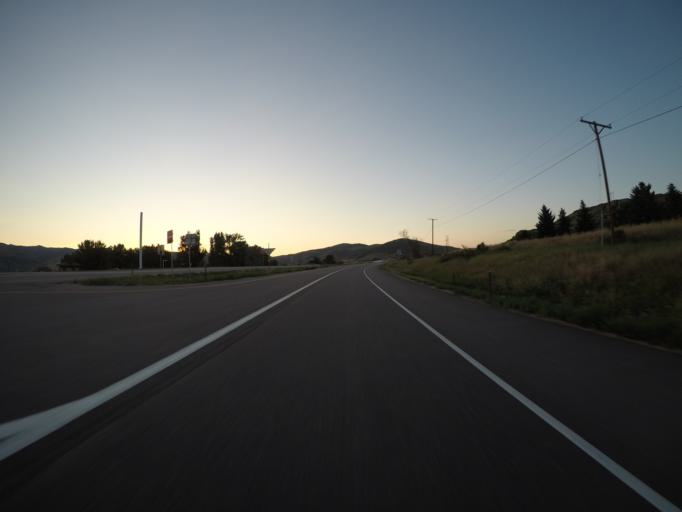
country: US
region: Colorado
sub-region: Larimer County
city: Laporte
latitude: 40.6639
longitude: -105.1884
